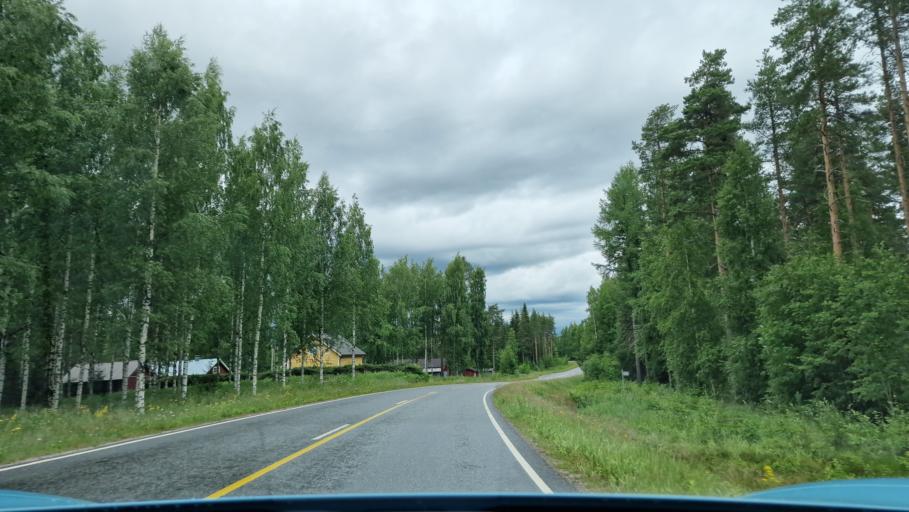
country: FI
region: Southern Ostrobothnia
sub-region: Jaerviseutu
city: Soini
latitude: 62.6926
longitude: 24.4599
